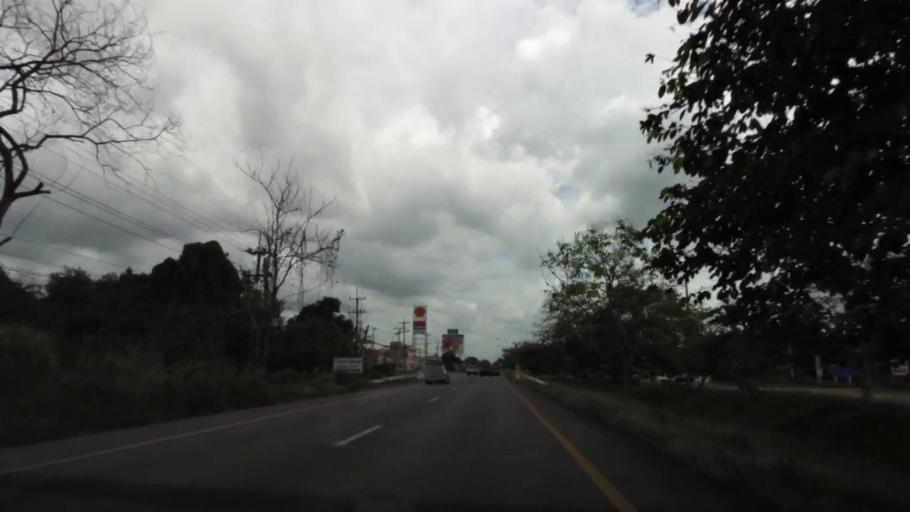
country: TH
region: Rayong
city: Klaeng
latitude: 12.7827
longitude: 101.6906
